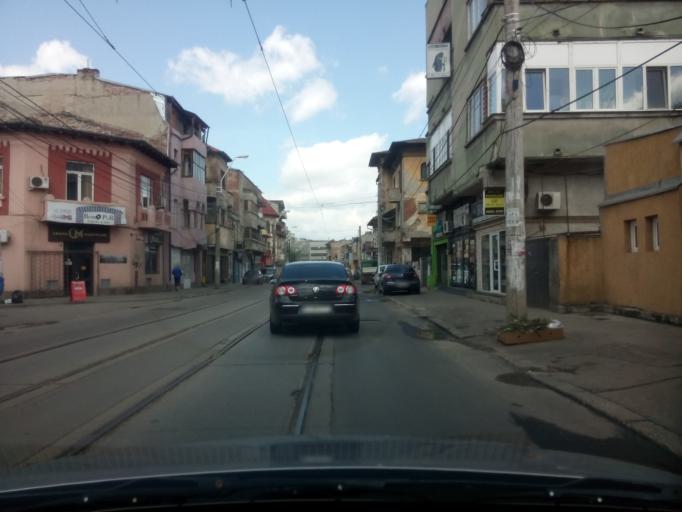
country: RO
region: Bucuresti
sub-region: Municipiul Bucuresti
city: Bucharest
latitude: 44.4529
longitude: 26.1204
